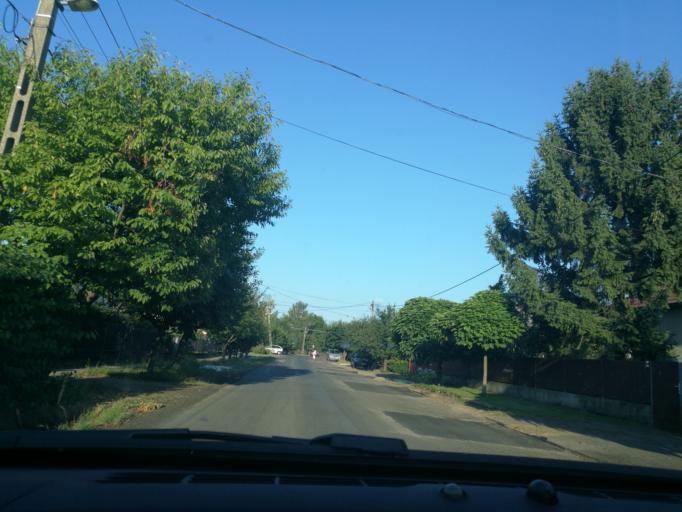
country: HU
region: Szabolcs-Szatmar-Bereg
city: Kotaj
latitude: 48.0043
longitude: 21.7405
